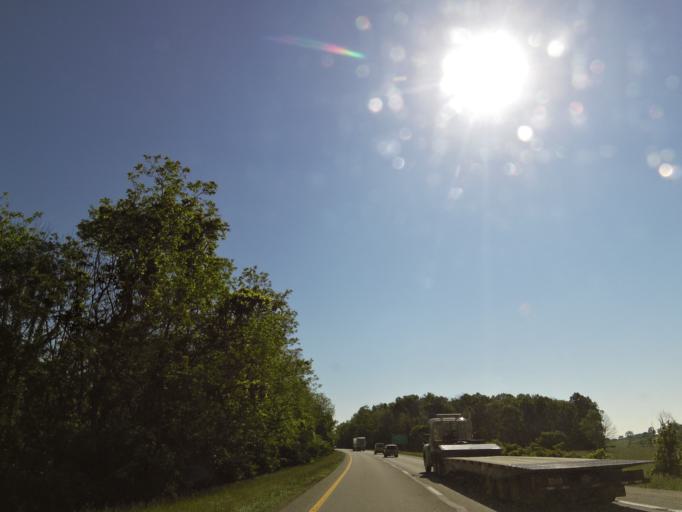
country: US
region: Kentucky
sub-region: Franklin County
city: Frankfort
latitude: 38.1519
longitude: -84.9407
